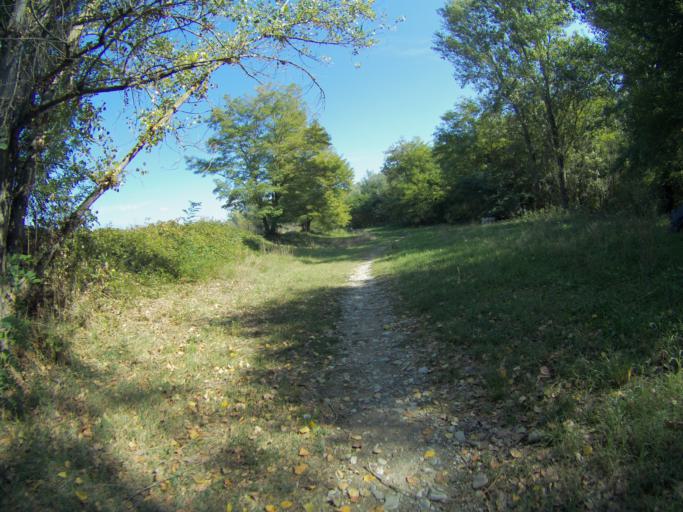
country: IT
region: Emilia-Romagna
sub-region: Provincia di Reggio Emilia
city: Forche
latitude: 44.6459
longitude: 10.5905
